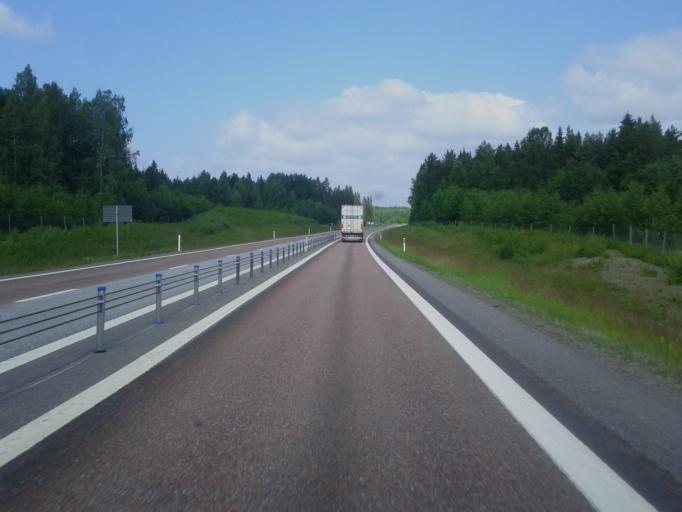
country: SE
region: Vaesterbotten
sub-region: Skelleftea Kommun
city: Skelleftea
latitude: 64.7178
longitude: 20.9889
